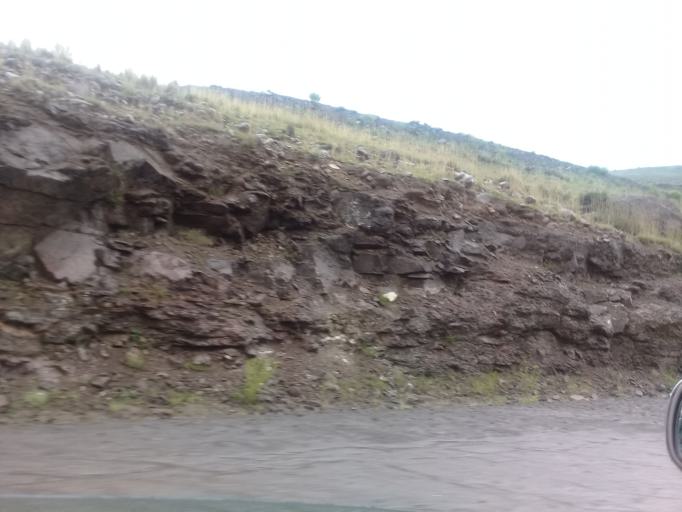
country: LS
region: Mokhotlong
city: Mokhotlong
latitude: -29.3320
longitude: 29.0255
